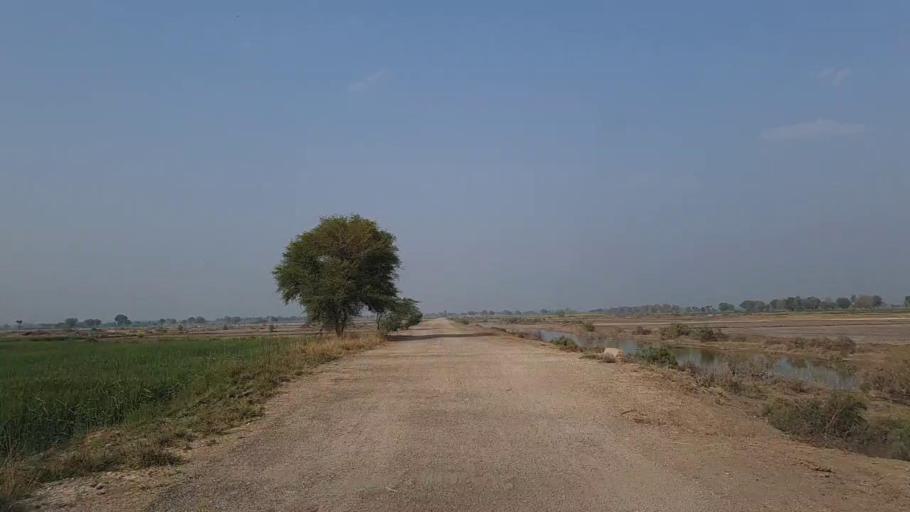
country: PK
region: Sindh
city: Nawabshah
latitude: 26.3394
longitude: 68.4738
